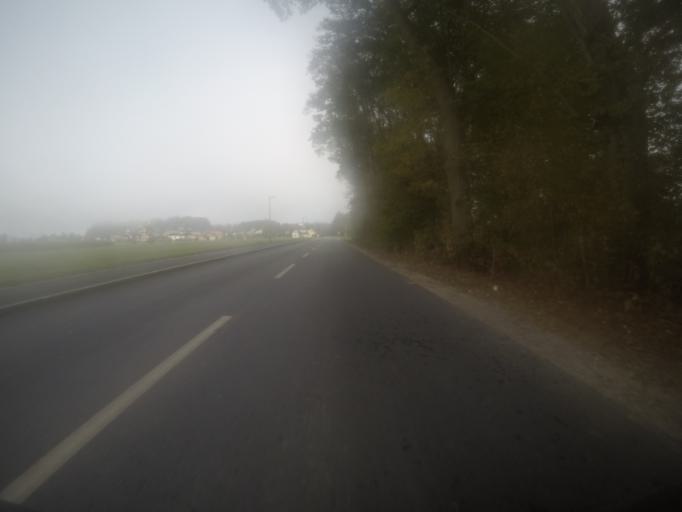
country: SI
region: Domzale
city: Dob
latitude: 46.1625
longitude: 14.6271
